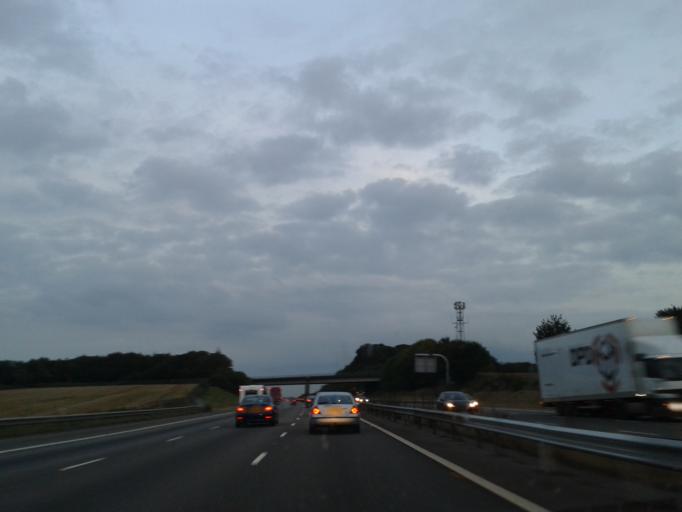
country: GB
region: England
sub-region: Oxfordshire
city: Somerton
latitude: 51.9684
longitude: -1.2485
